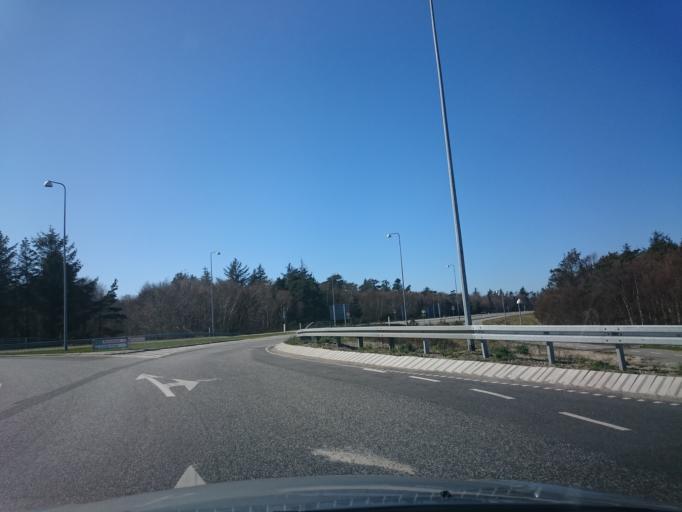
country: DK
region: North Denmark
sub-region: Hjorring Kommune
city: Hirtshals
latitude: 57.5780
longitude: 9.9862
